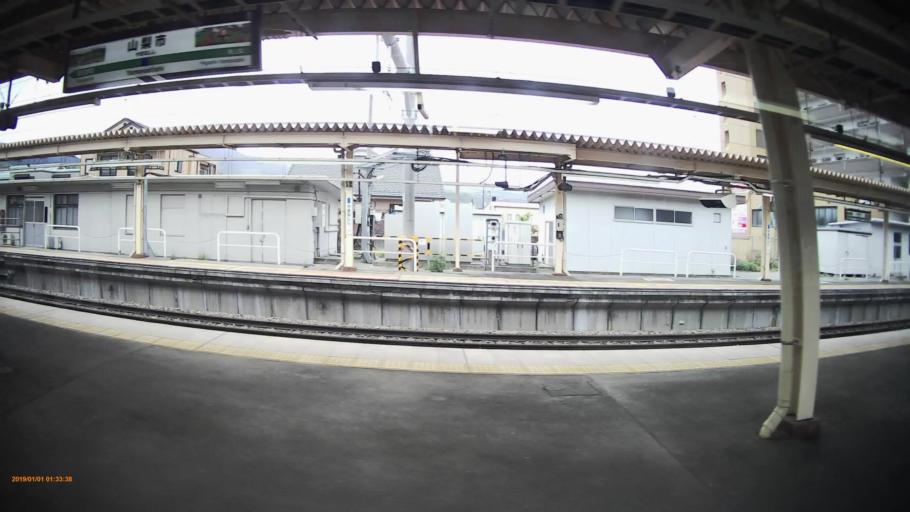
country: JP
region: Yamanashi
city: Enzan
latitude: 35.6851
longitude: 138.6825
